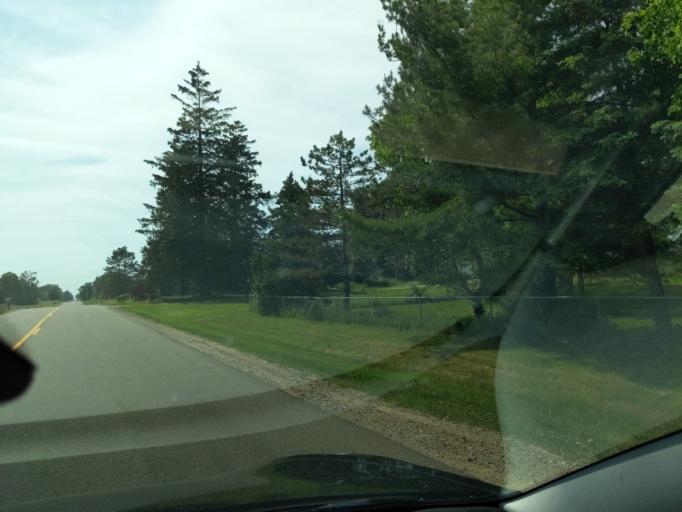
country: US
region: Michigan
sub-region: Eaton County
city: Grand Ledge
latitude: 42.7121
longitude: -84.8377
